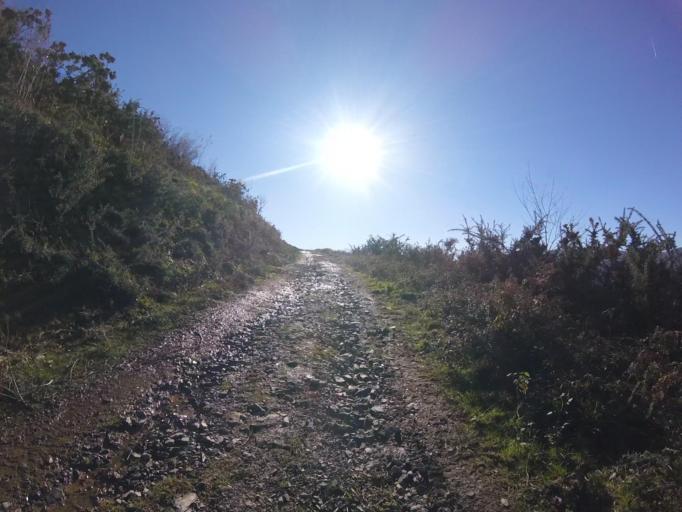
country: FR
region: Aquitaine
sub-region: Departement des Pyrenees-Atlantiques
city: Urrugne
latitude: 43.3268
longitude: -1.7302
